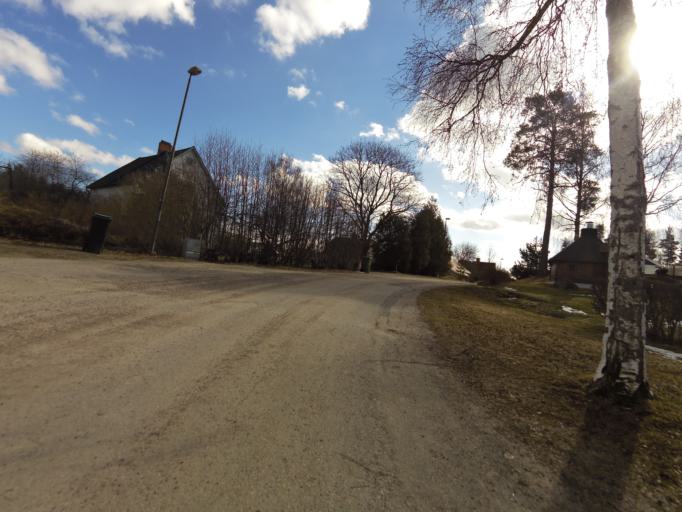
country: SE
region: Gaevleborg
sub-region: Hofors Kommun
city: Hofors
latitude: 60.5358
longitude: 16.2989
